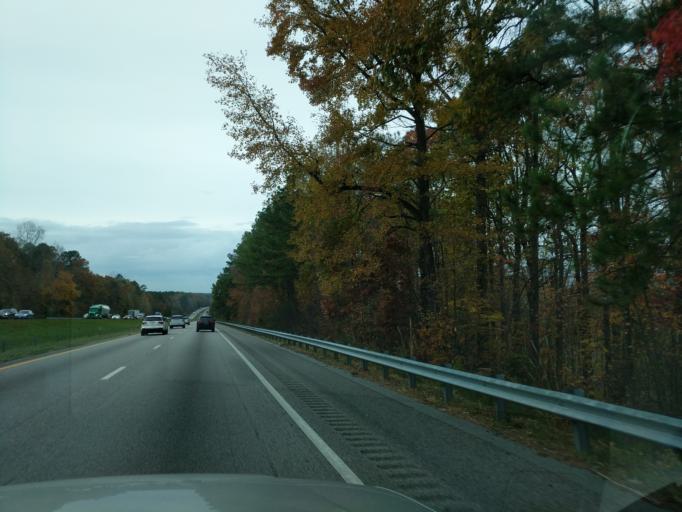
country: US
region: South Carolina
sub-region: Laurens County
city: Clinton
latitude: 34.4812
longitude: -81.8234
